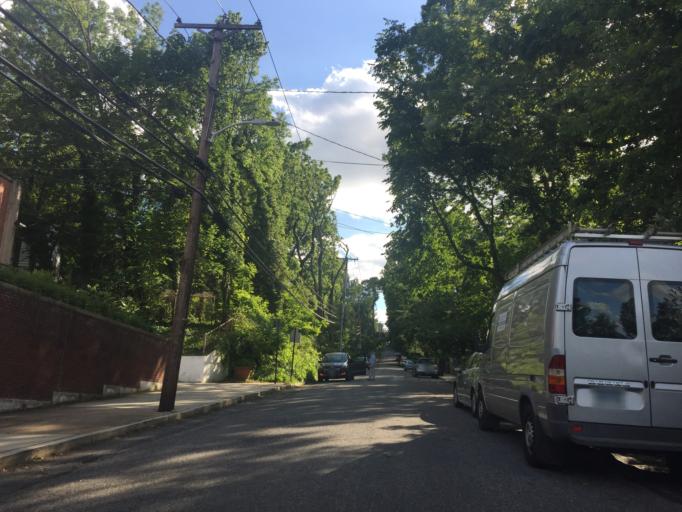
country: US
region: Maryland
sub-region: Baltimore County
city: Lutherville
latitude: 39.3661
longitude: -76.6551
